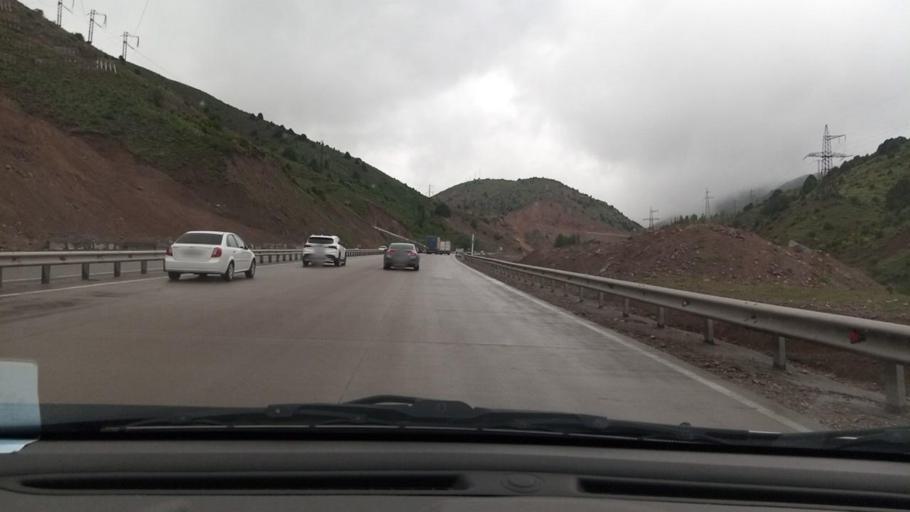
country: UZ
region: Toshkent
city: Angren
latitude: 41.0592
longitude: 70.5618
